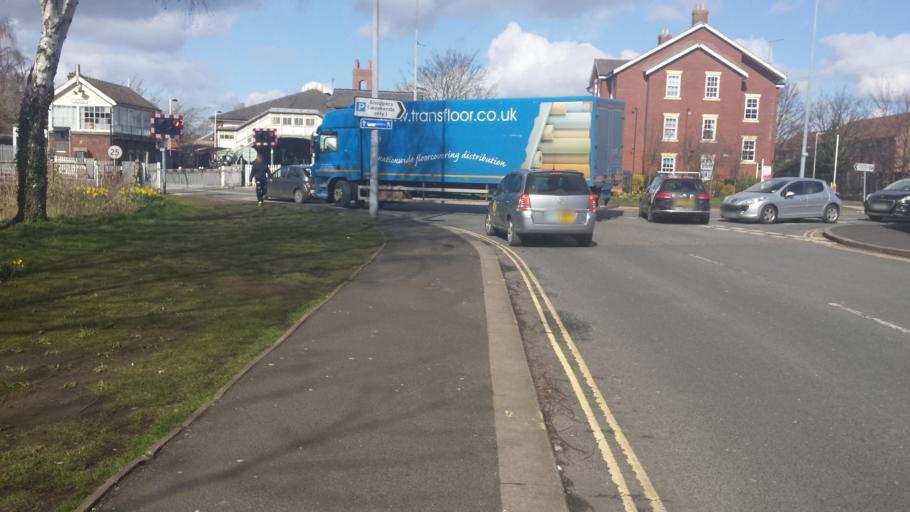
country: GB
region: England
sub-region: East Riding of Yorkshire
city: Beverley
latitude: 53.8411
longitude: -0.4225
